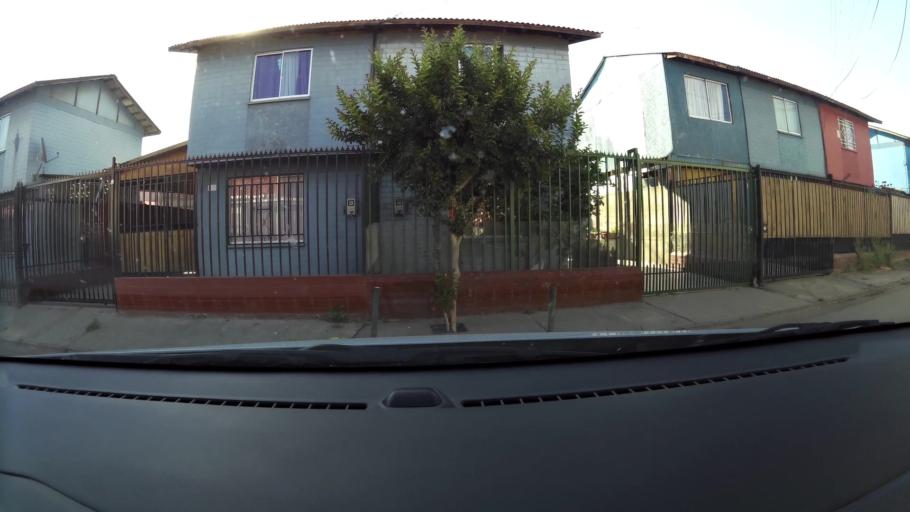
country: CL
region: Santiago Metropolitan
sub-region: Provincia de Maipo
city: San Bernardo
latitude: -33.6009
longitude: -70.6810
